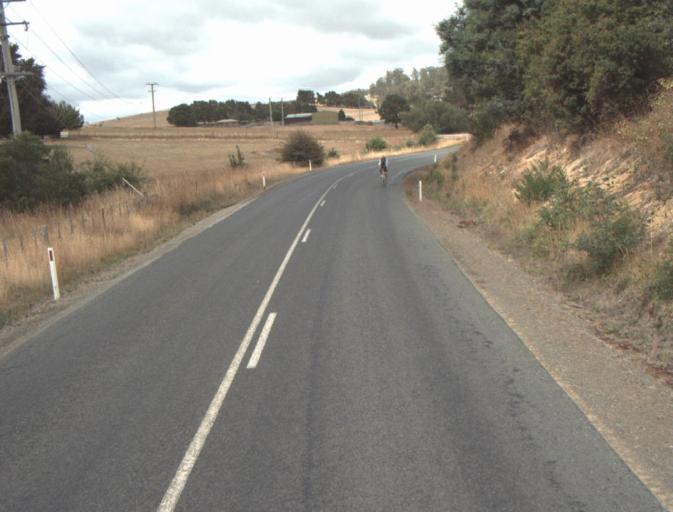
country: AU
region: Tasmania
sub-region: Launceston
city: Mayfield
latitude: -41.1909
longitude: 147.2214
